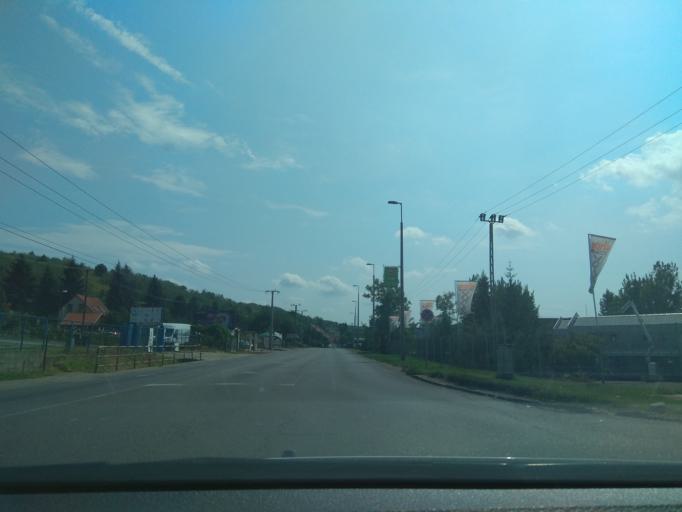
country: HU
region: Heves
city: Andornaktalya
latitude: 47.8728
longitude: 20.4028
